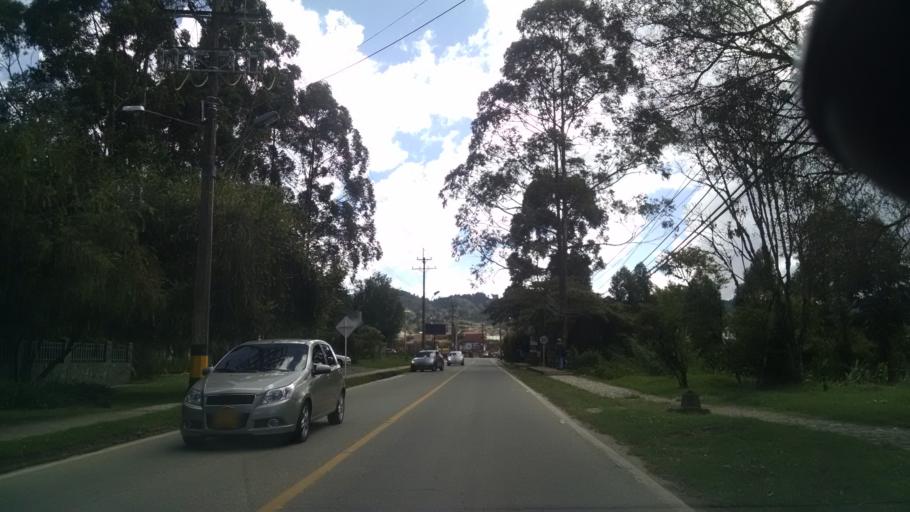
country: CO
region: Antioquia
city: El Retiro
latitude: 6.0662
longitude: -75.5006
